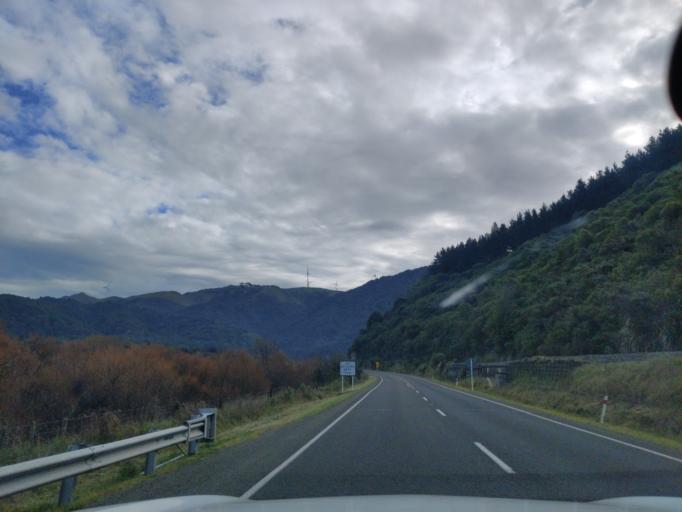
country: NZ
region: Manawatu-Wanganui
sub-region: Palmerston North City
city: Palmerston North
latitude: -40.3386
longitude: 175.8245
